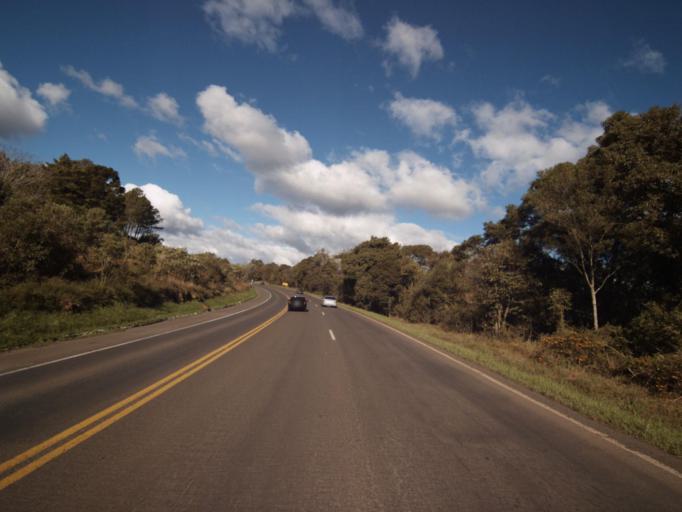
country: BR
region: Santa Catarina
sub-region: Joacaba
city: Joacaba
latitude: -27.1639
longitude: -51.5680
